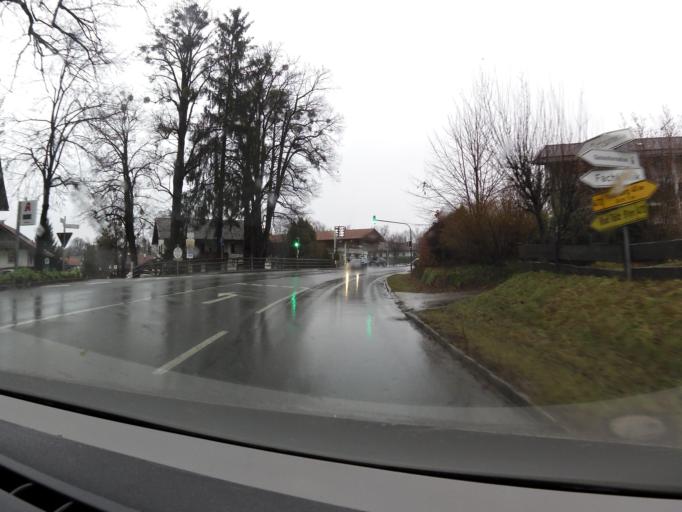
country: DE
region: Bavaria
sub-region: Upper Bavaria
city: Bad Heilbrunn
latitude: 47.7406
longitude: 11.4521
